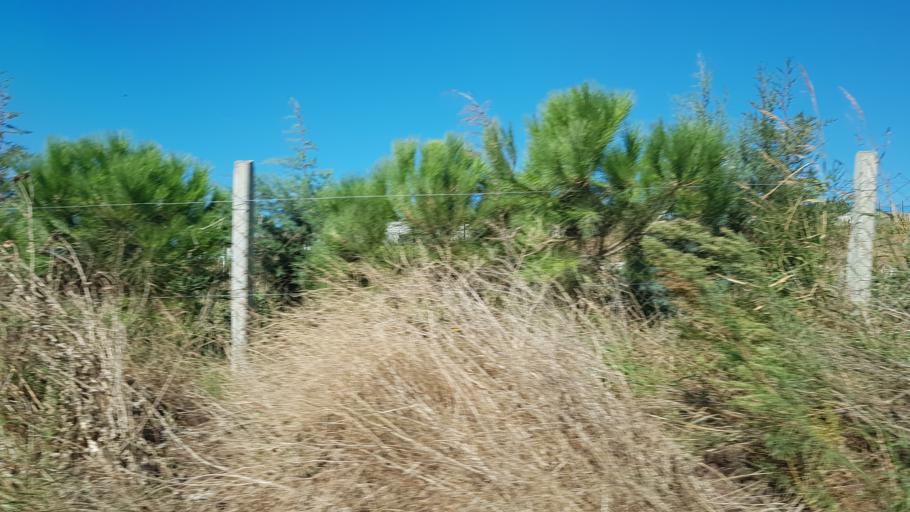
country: TR
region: Tekirdag
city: Corlu
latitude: 41.0308
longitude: 27.8122
